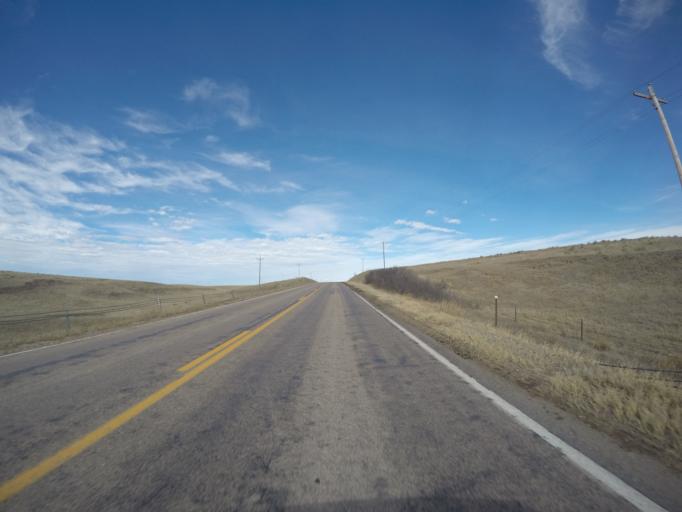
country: US
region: Nebraska
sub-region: Franklin County
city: Franklin
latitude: 40.1415
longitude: -98.9524
